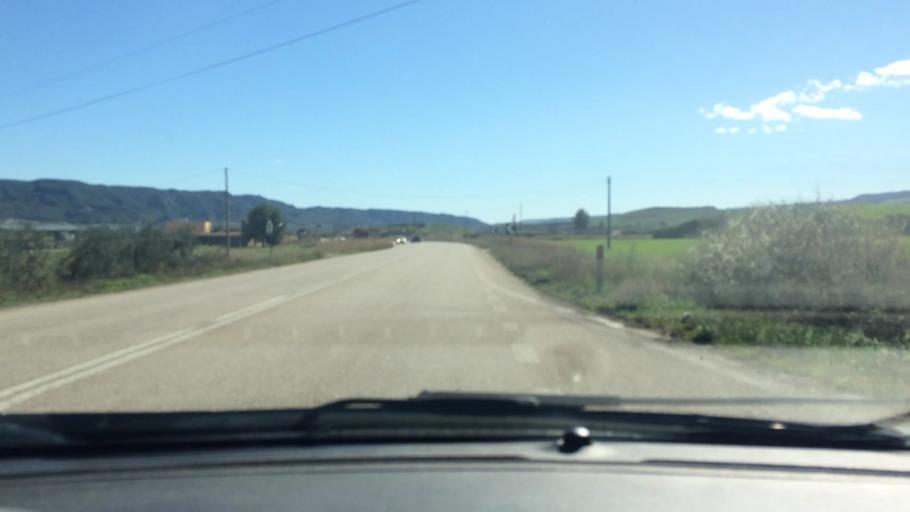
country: IT
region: Basilicate
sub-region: Provincia di Matera
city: Montescaglioso
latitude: 40.5334
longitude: 16.6072
